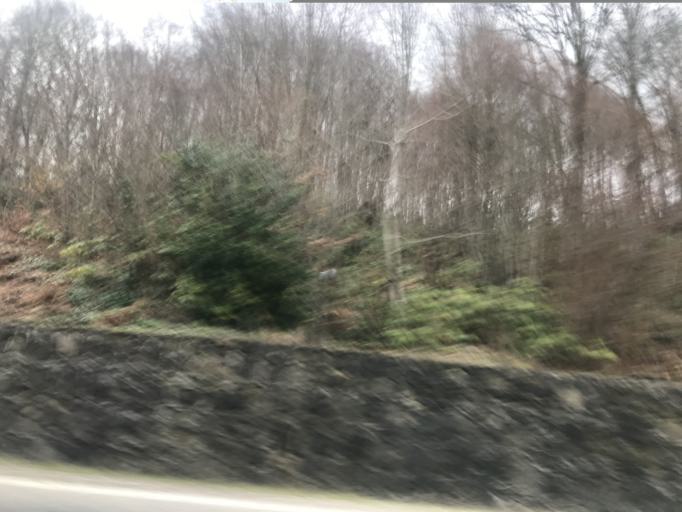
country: TR
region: Bartin
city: Amasra
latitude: 41.7138
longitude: 32.3927
